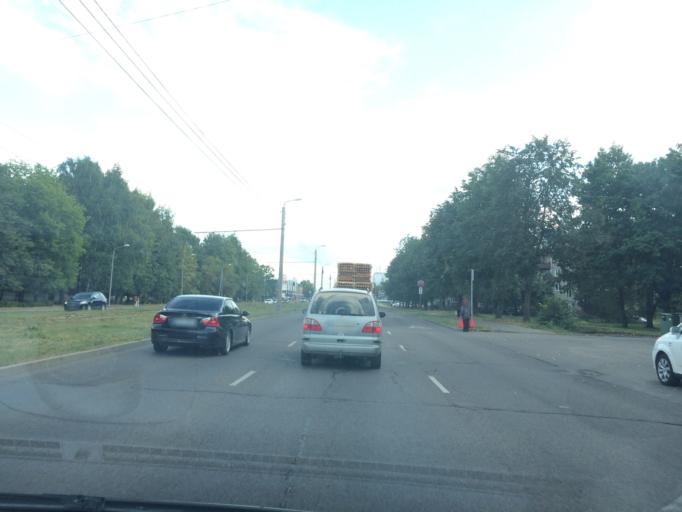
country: LV
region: Kekava
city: Balozi
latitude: 56.9077
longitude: 24.1849
